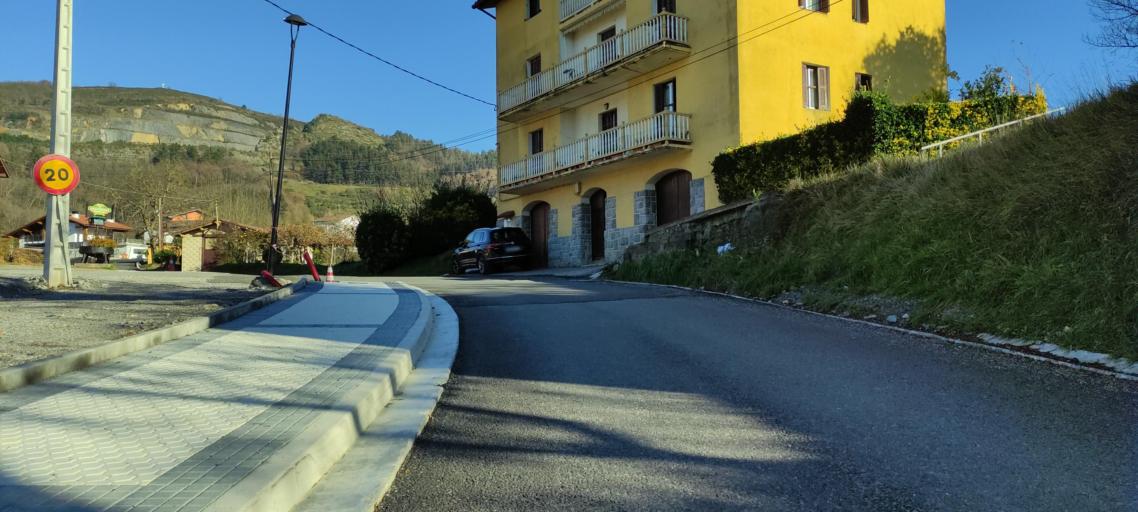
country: ES
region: Basque Country
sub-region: Provincia de Guipuzcoa
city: Andoain
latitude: 43.2242
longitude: -2.0177
